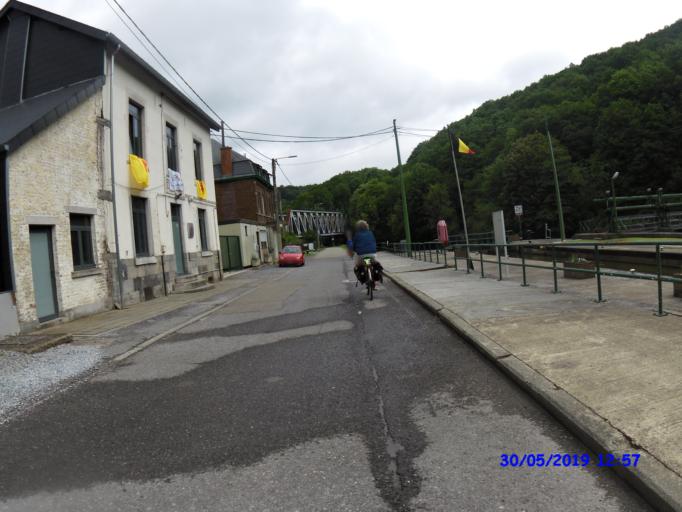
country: BE
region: Wallonia
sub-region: Province du Hainaut
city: Thuin
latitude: 50.3436
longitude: 4.2935
